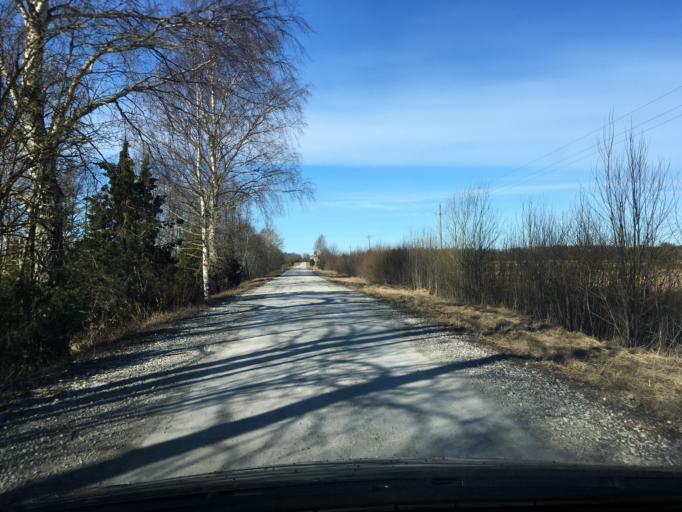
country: EE
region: Laeaene
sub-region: Lihula vald
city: Lihula
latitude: 58.5675
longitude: 23.6824
